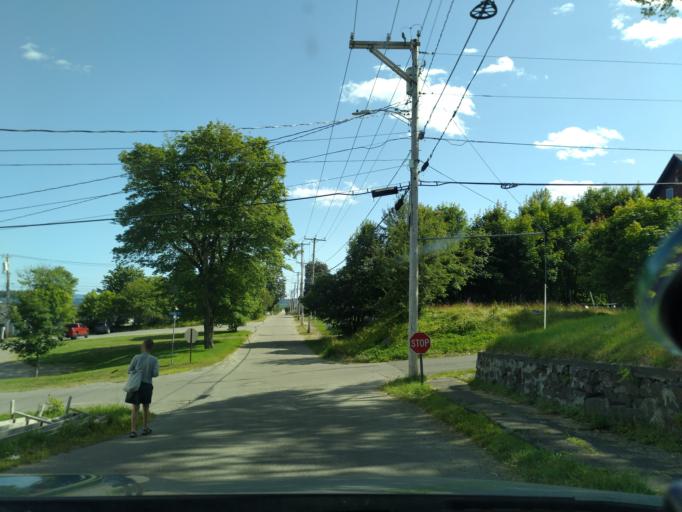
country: US
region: Maine
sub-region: Washington County
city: Eastport
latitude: 44.8608
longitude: -66.9843
